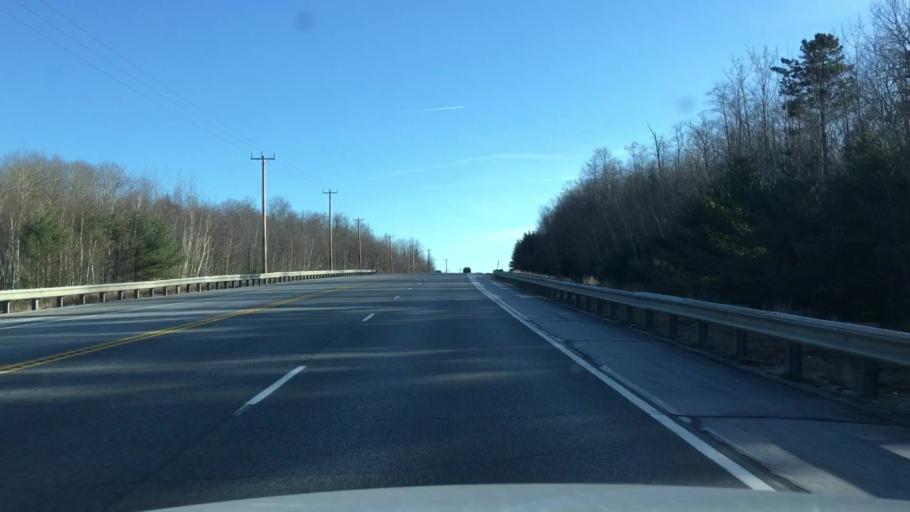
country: US
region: Maine
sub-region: Hancock County
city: Dedham
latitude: 44.6927
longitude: -68.5892
